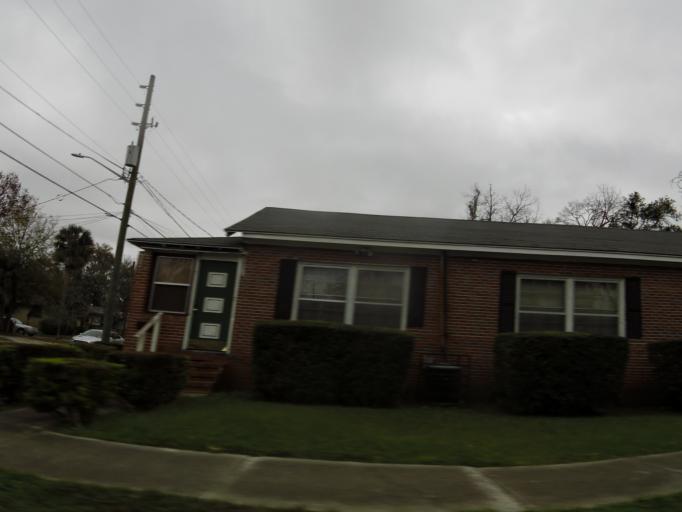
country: US
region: Florida
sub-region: Duval County
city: Jacksonville
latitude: 30.3584
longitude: -81.6881
